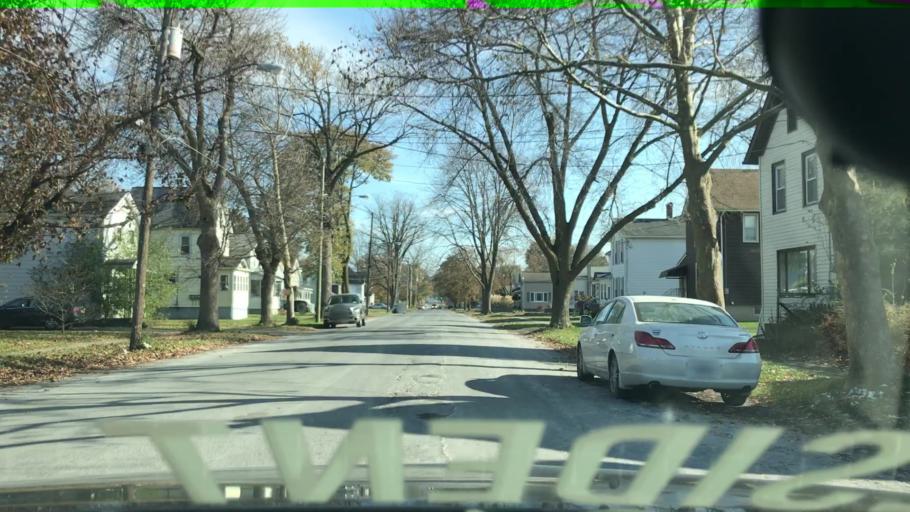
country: US
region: New York
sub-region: Cayuga County
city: Auburn
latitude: 42.9399
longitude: -76.5770
